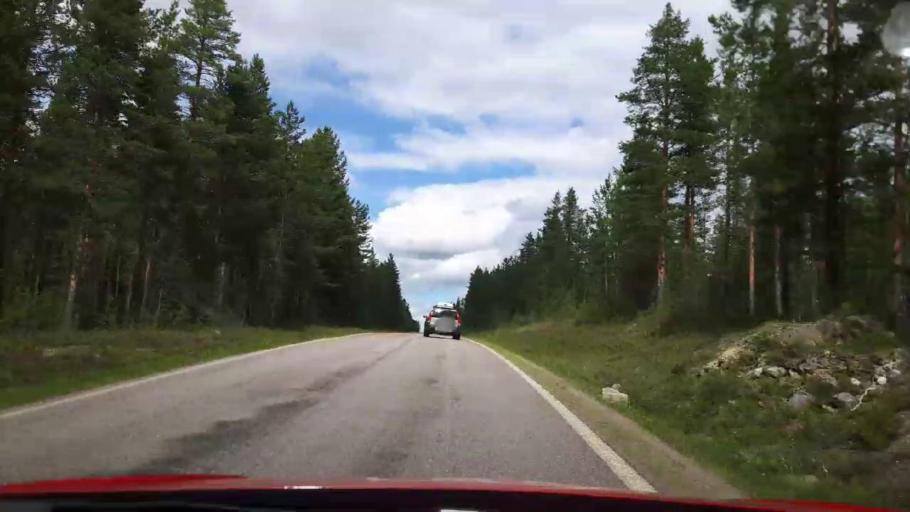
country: NO
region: Hedmark
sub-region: Trysil
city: Innbygda
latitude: 61.8367
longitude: 12.9571
